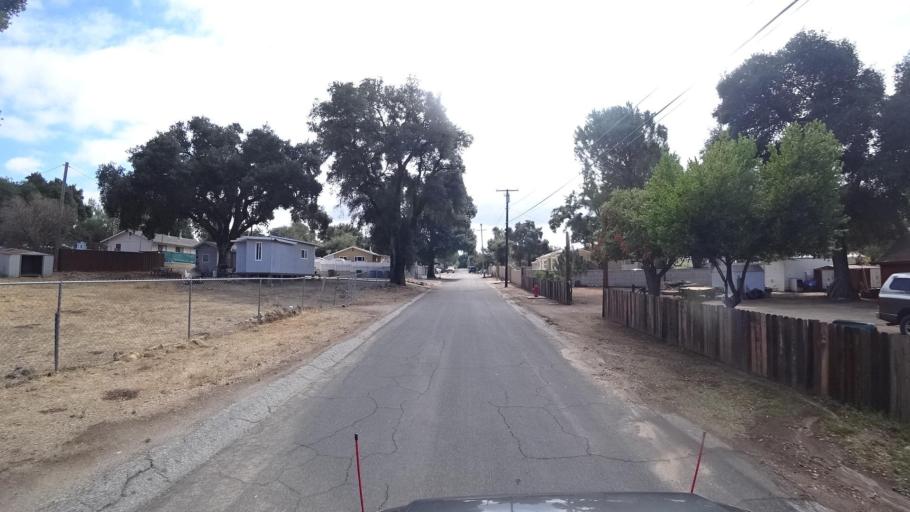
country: US
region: California
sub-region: San Diego County
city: Campo
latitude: 32.6853
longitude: -116.5137
